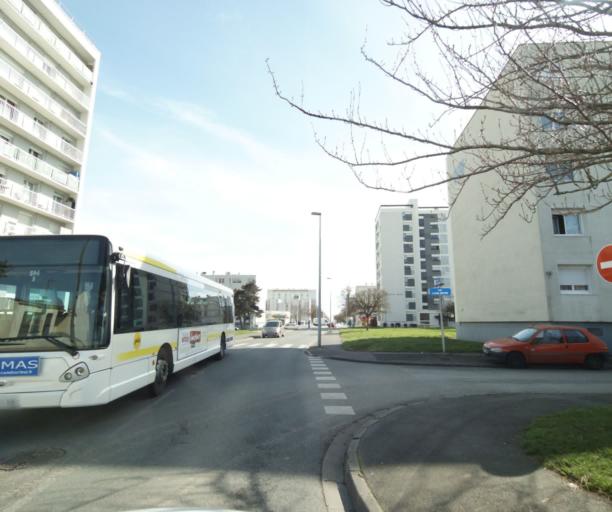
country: FR
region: Poitou-Charentes
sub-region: Departement de la Charente-Maritime
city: La Rochelle
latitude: 46.1699
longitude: -1.1727
